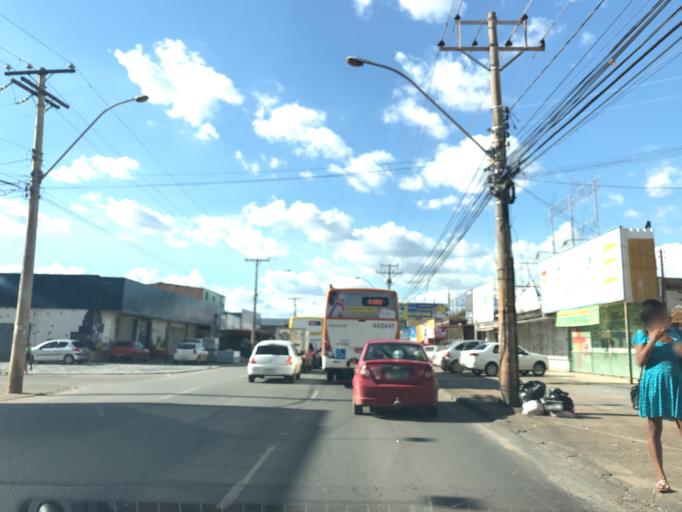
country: BR
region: Federal District
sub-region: Brasilia
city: Brasilia
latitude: -15.8057
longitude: -48.0702
